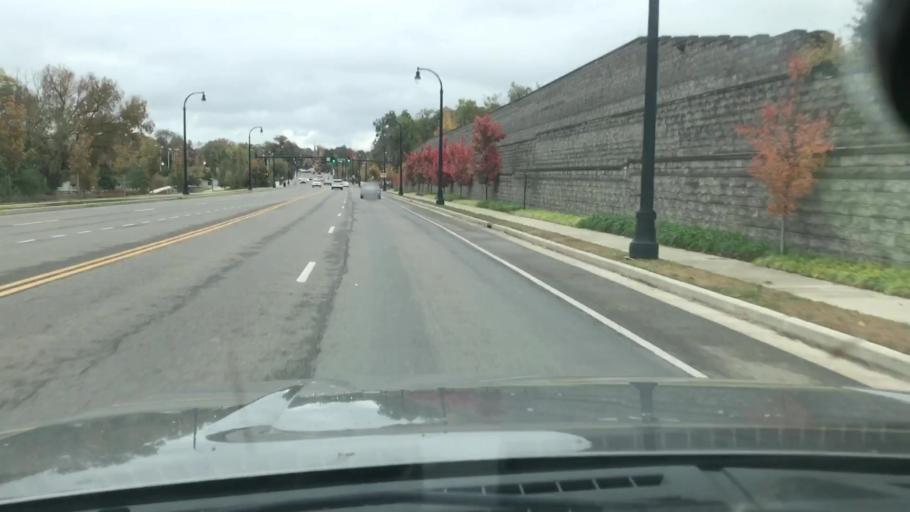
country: US
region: Tennessee
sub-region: Williamson County
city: Franklin
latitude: 35.9305
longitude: -86.8763
